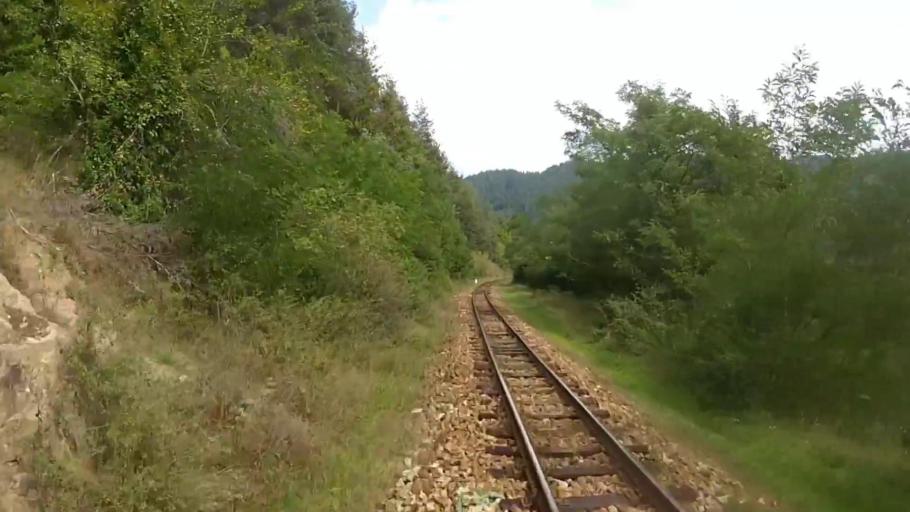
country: BG
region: Blagoevgrad
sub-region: Obshtina Yakoruda
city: Yakoruda
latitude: 42.0409
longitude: 23.7181
